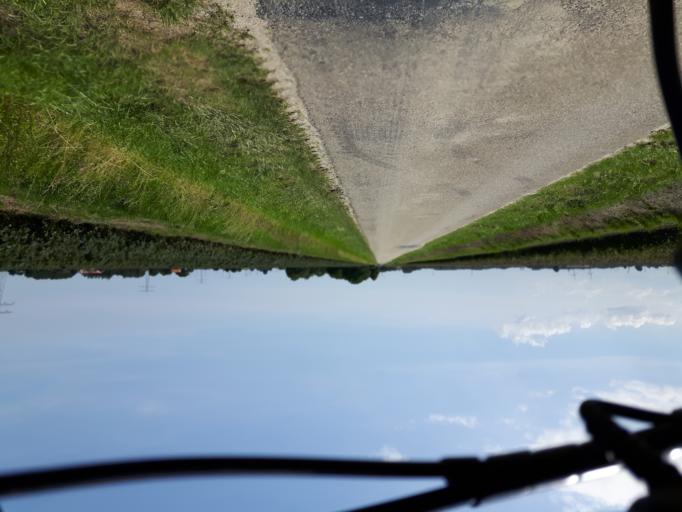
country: NL
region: Zeeland
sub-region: Gemeente Borsele
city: Borssele
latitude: 51.4805
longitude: 3.7756
